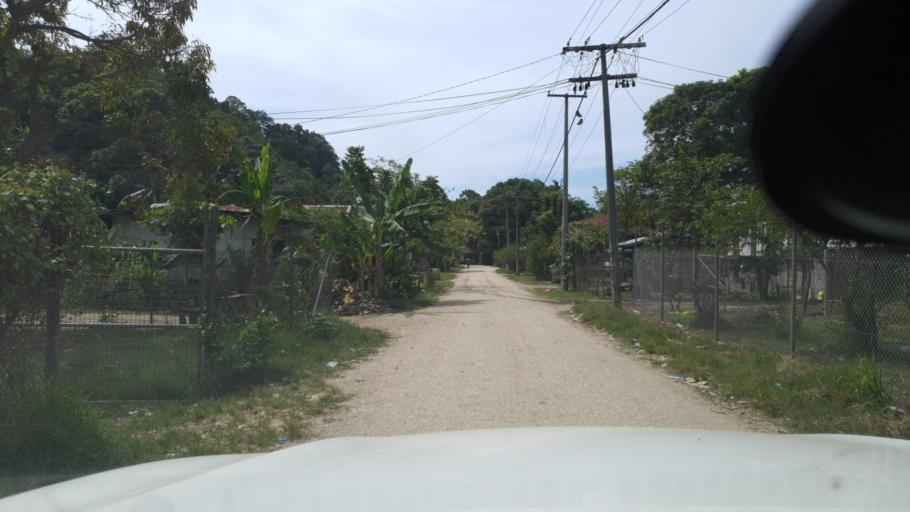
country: SB
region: Guadalcanal
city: Honiara
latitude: -9.4294
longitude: 159.9190
